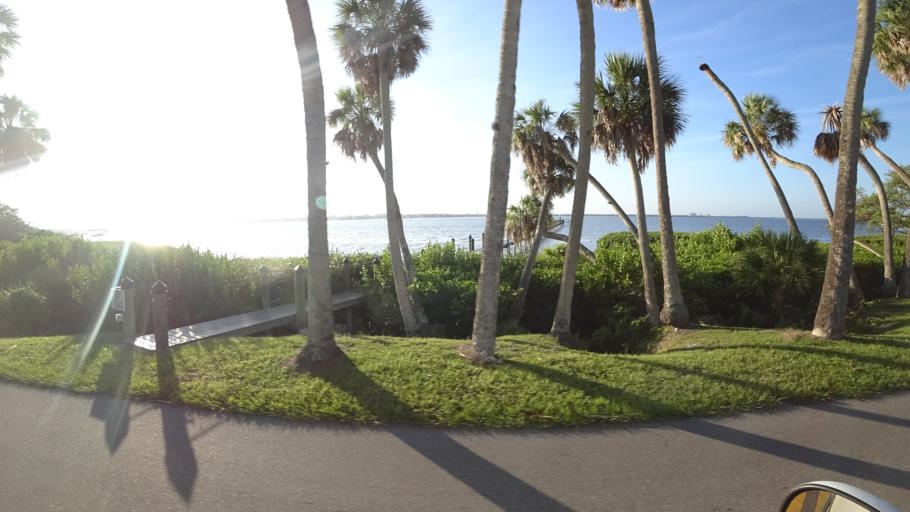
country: US
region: Florida
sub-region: Manatee County
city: Memphis
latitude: 27.5700
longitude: -82.5803
